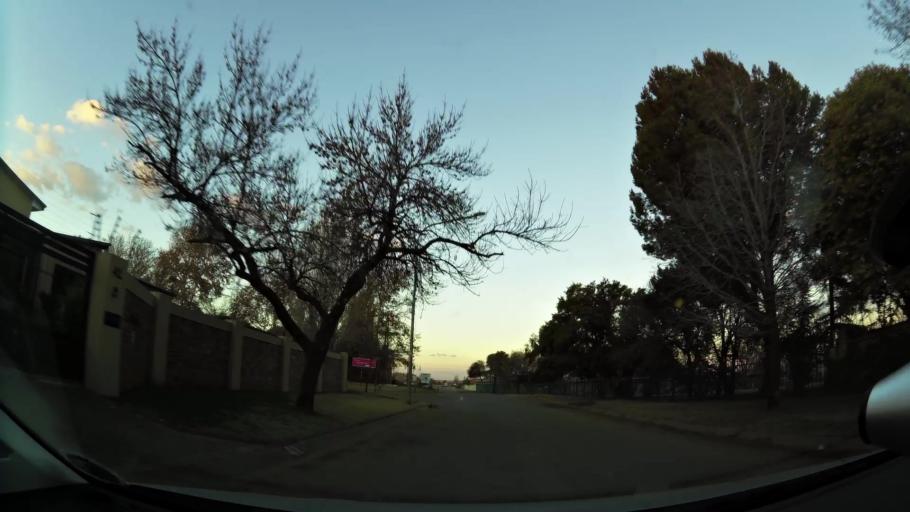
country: ZA
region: North-West
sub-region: Dr Kenneth Kaunda District Municipality
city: Potchefstroom
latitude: -26.7224
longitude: 27.1226
